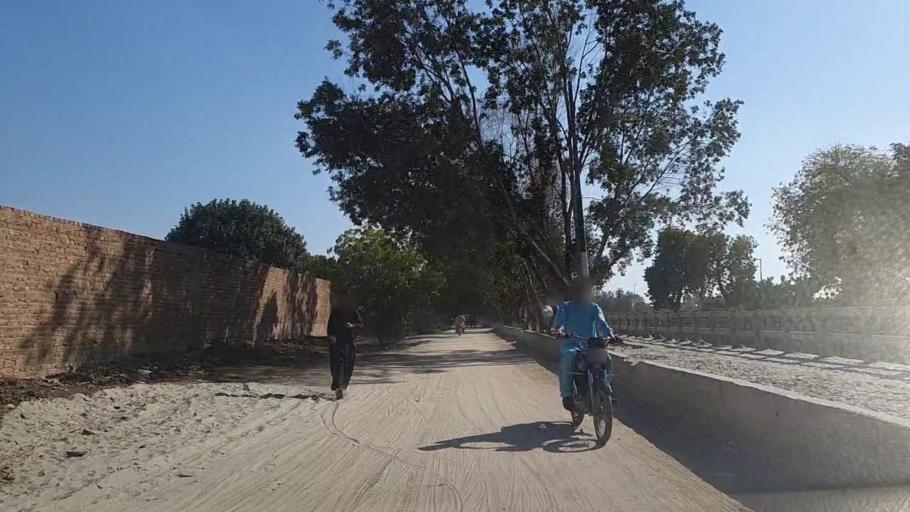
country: PK
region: Sindh
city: Nawabshah
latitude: 26.2468
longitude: 68.4214
